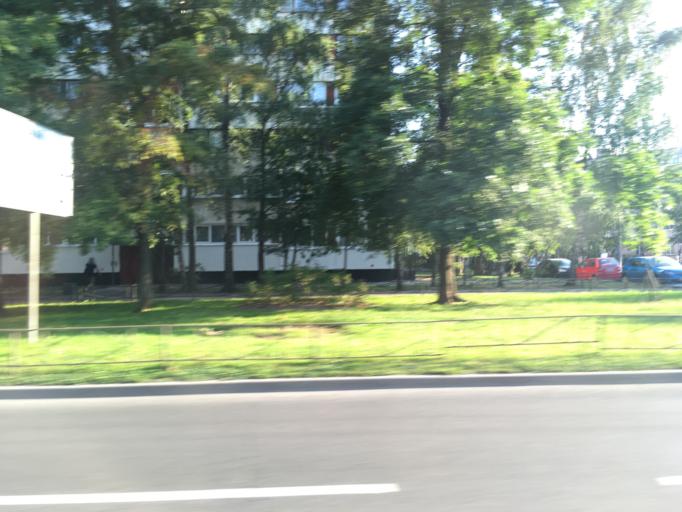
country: RU
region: St.-Petersburg
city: Komendantsky aerodrom
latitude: 60.0110
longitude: 30.2831
